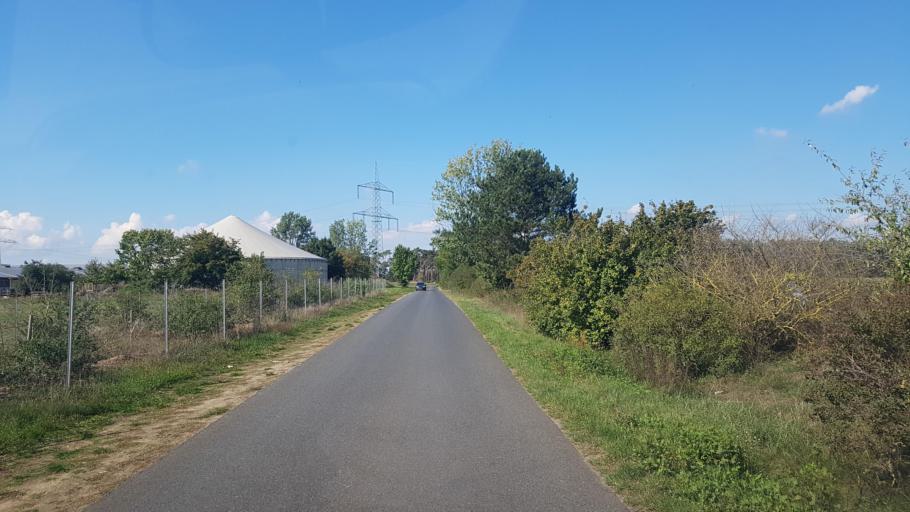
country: DE
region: Brandenburg
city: Ihlow
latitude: 51.8360
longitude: 13.3556
